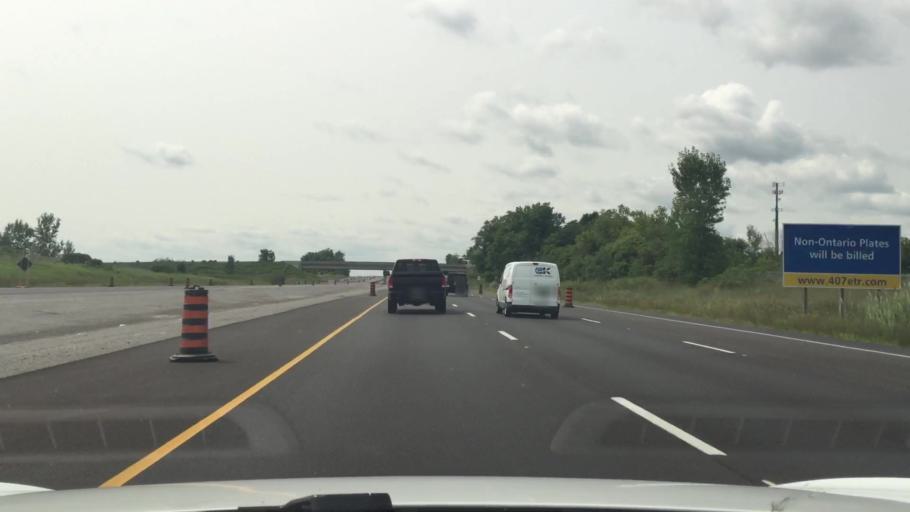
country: CA
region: Ontario
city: Pickering
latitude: 43.9095
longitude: -79.1290
